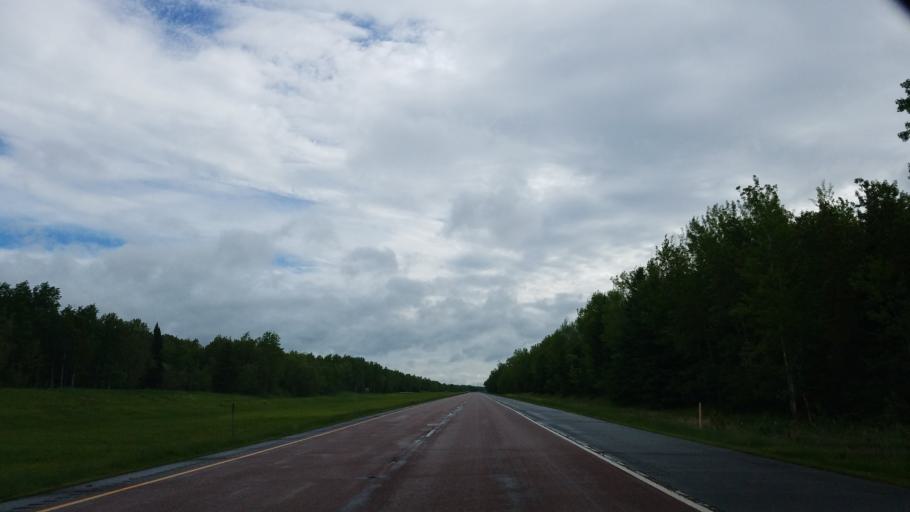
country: US
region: Minnesota
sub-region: Saint Louis County
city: Arnold
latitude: 46.8733
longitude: -91.9499
